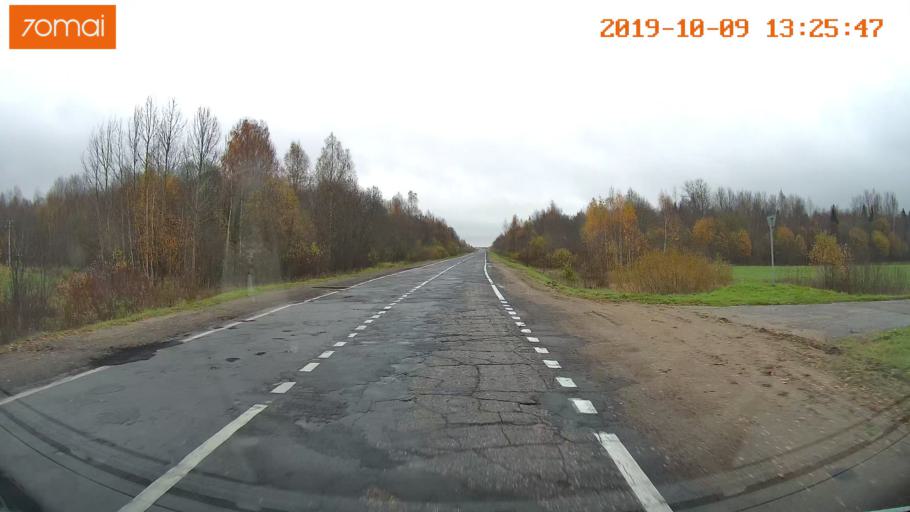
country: RU
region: Jaroslavl
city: Lyubim
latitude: 58.3257
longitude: 40.9161
